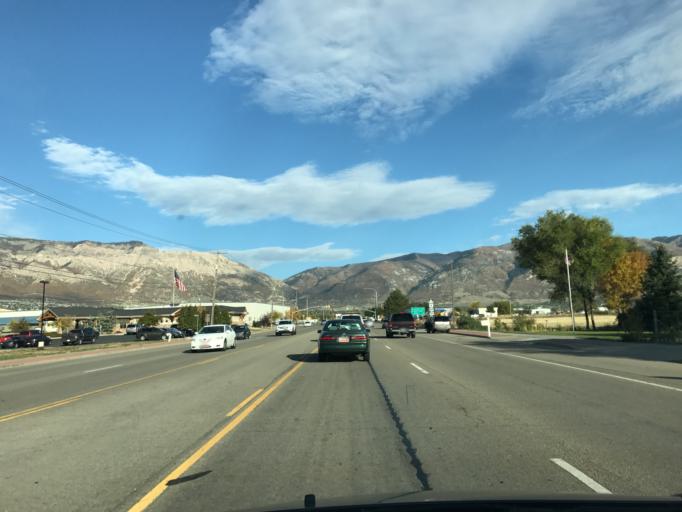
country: US
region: Utah
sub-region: Weber County
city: Pleasant View
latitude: 41.3069
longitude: -112.0085
